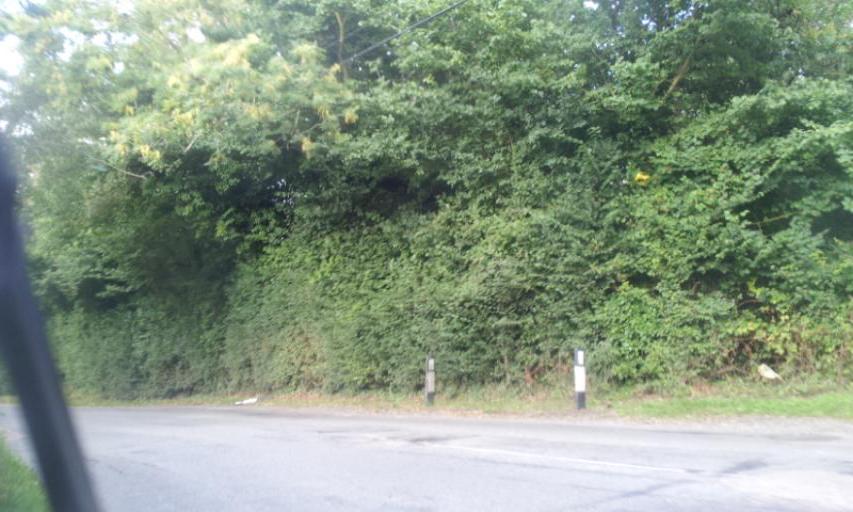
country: GB
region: England
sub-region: Kent
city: Tonbridge
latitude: 51.1859
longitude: 0.3173
